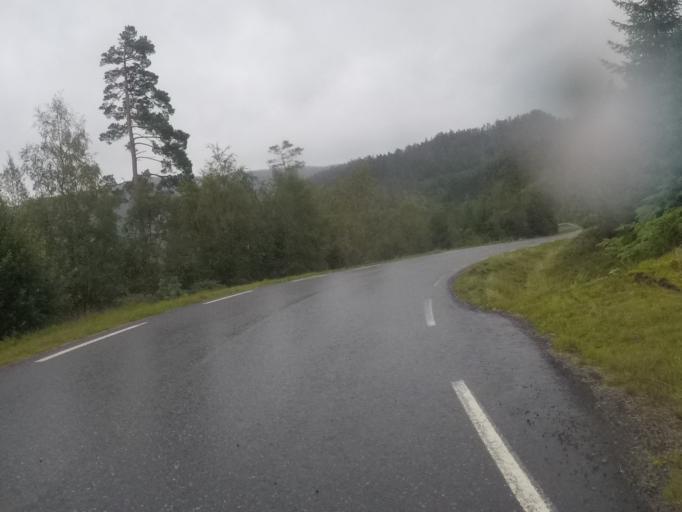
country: NO
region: Vest-Agder
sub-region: Lyngdal
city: Lyngdal
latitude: 58.2386
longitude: 7.1473
